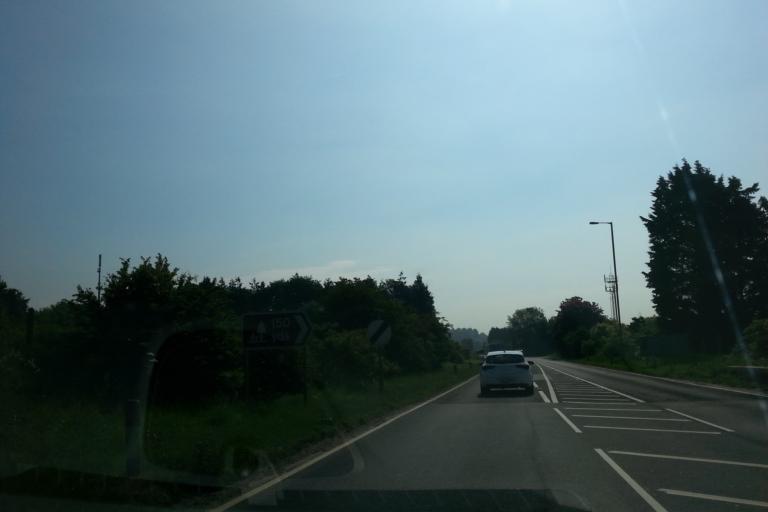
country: GB
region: England
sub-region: Peterborough
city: Wansford
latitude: 52.5846
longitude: -0.4091
